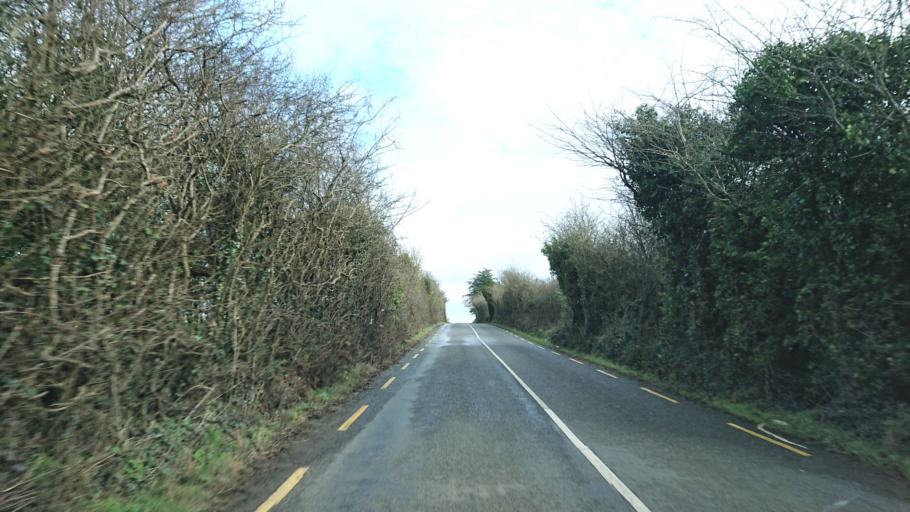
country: IE
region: Munster
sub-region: Waterford
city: Dunmore East
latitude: 52.2456
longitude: -6.8662
